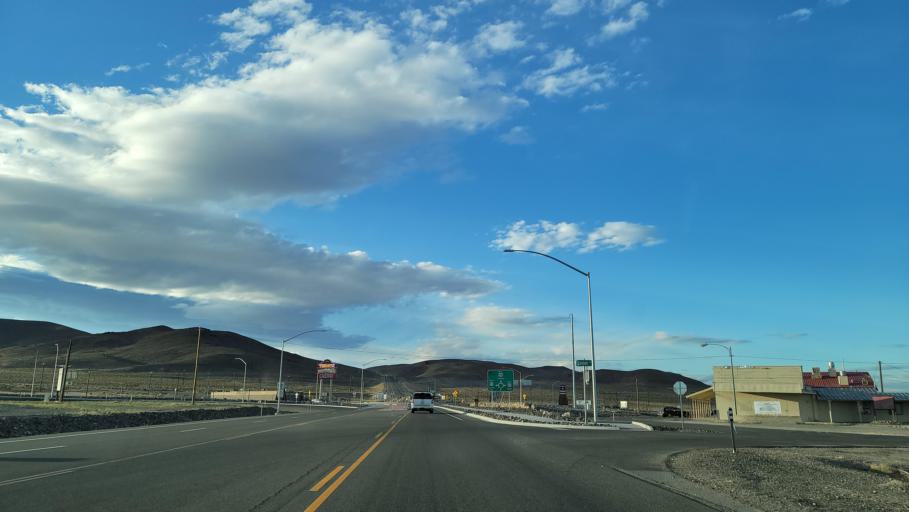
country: US
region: Nevada
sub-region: Lyon County
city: Silver Springs
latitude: 39.4145
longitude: -119.2254
